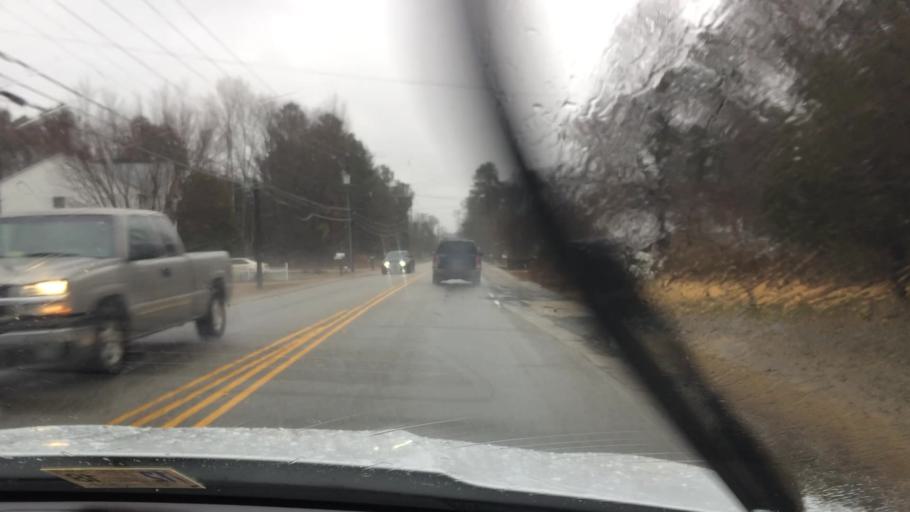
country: US
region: Virginia
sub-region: City of Williamsburg
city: Williamsburg
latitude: 37.2249
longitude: -76.6262
